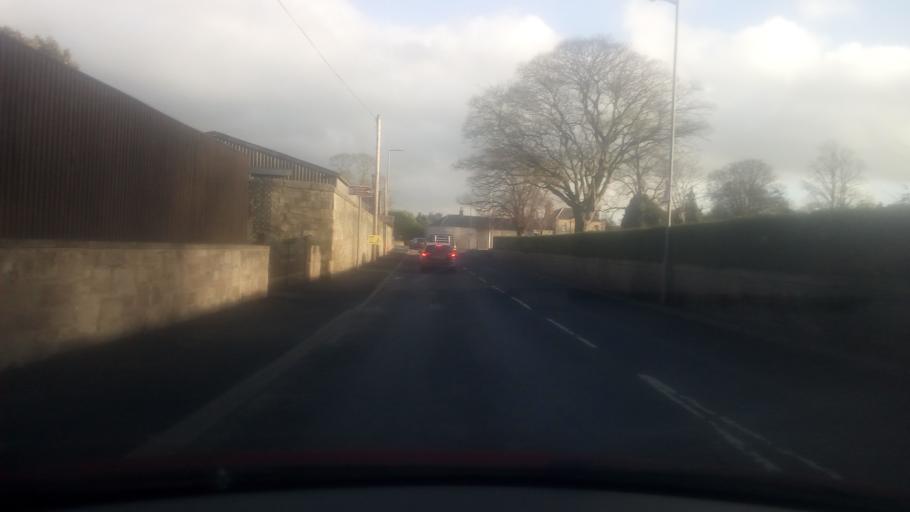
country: GB
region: Scotland
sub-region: The Scottish Borders
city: Kelso
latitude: 55.6015
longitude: -2.4272
